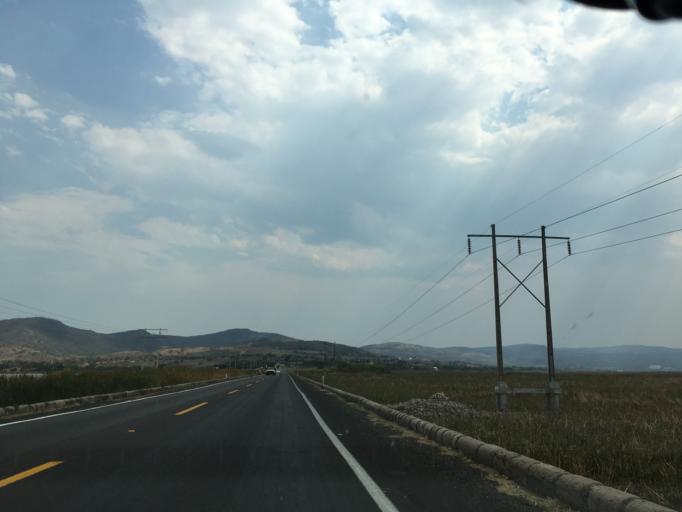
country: MX
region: Michoacan
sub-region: Cuitzeo
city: San Juan Benito Juarez (San Juan Tararameo)
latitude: 19.9340
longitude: -101.1391
